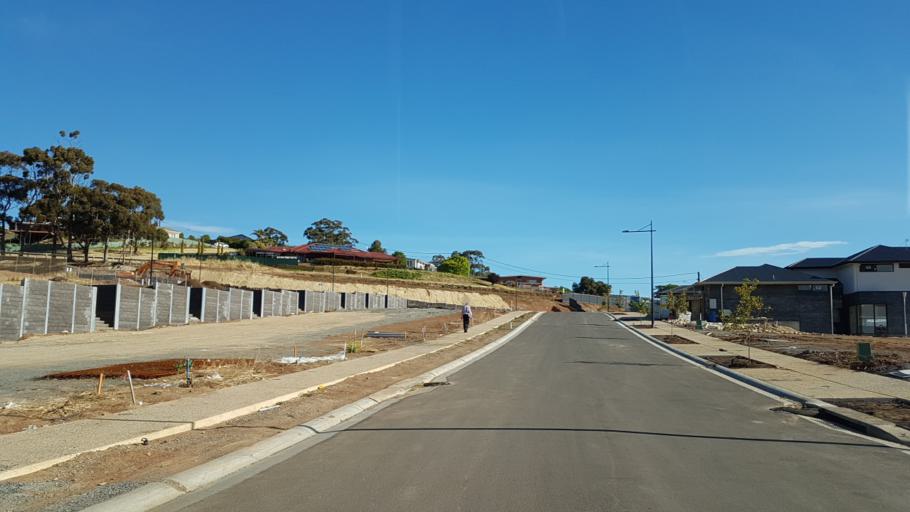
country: AU
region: South Australia
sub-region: Adelaide Hills
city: Adelaide Hills
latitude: -34.9062
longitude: 138.6872
